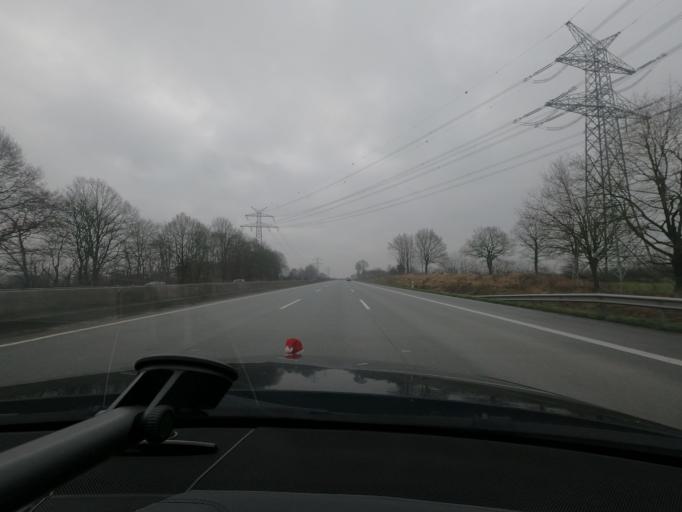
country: DE
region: Schleswig-Holstein
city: Alveslohe
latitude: 53.7808
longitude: 9.9410
